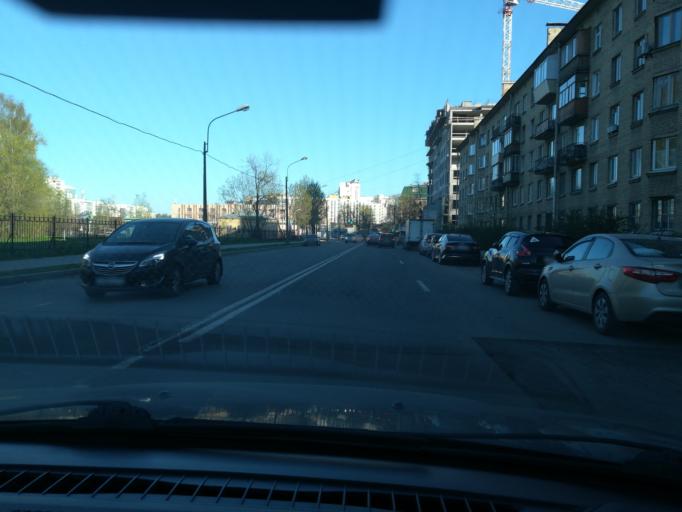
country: RU
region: St.-Petersburg
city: Vasyl'evsky Ostrov
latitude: 59.9400
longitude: 30.2431
